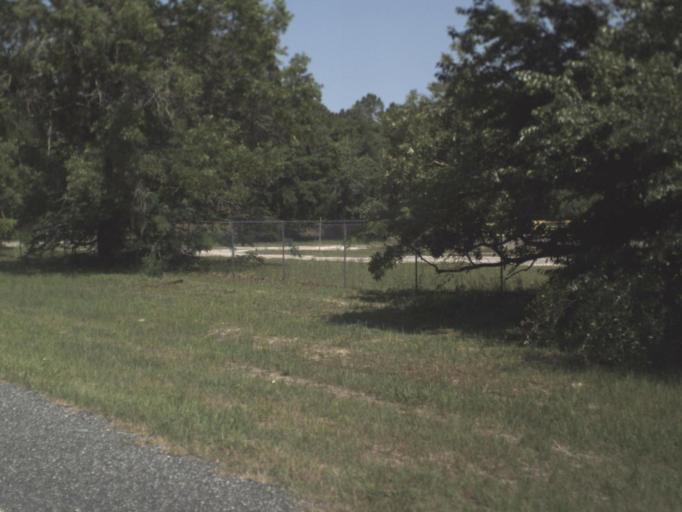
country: US
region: Florida
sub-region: Clay County
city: Middleburg
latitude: 29.9818
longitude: -81.9566
